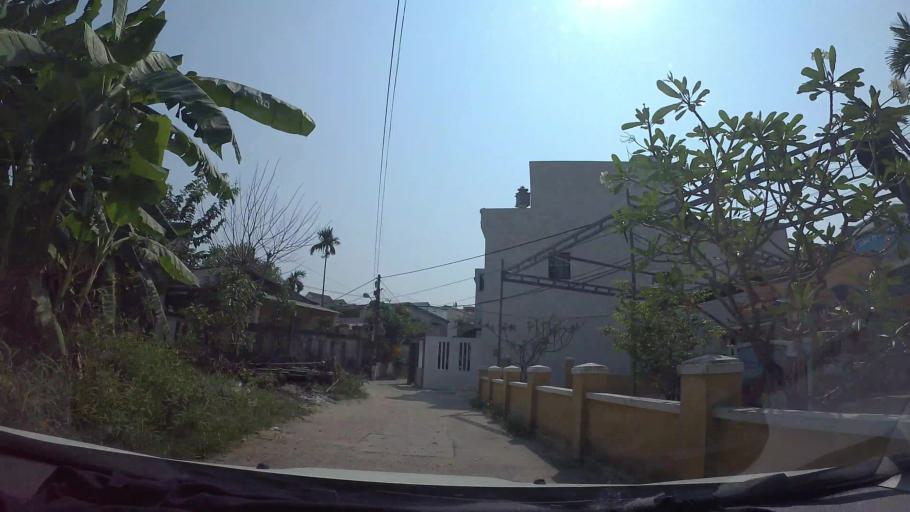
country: VN
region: Da Nang
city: Cam Le
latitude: 16.0119
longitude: 108.1968
